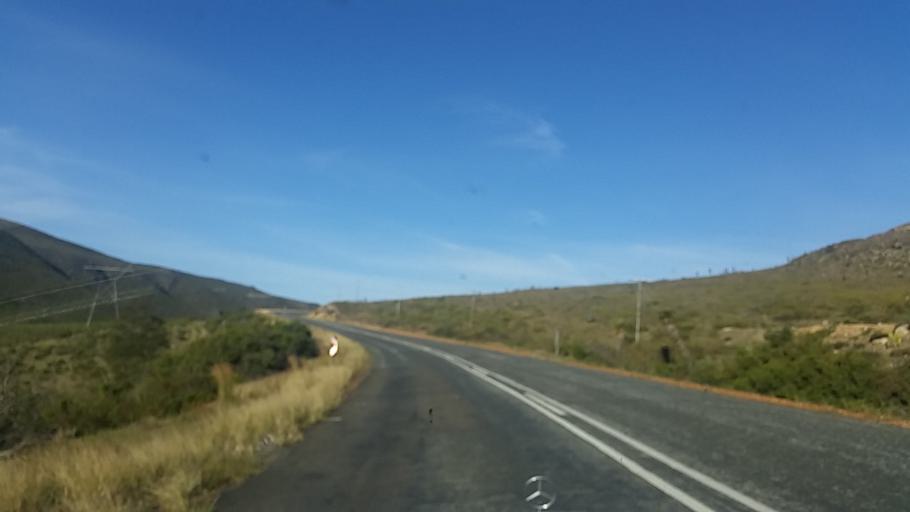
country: ZA
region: Western Cape
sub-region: Eden District Municipality
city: Knysna
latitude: -33.7431
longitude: 22.9994
